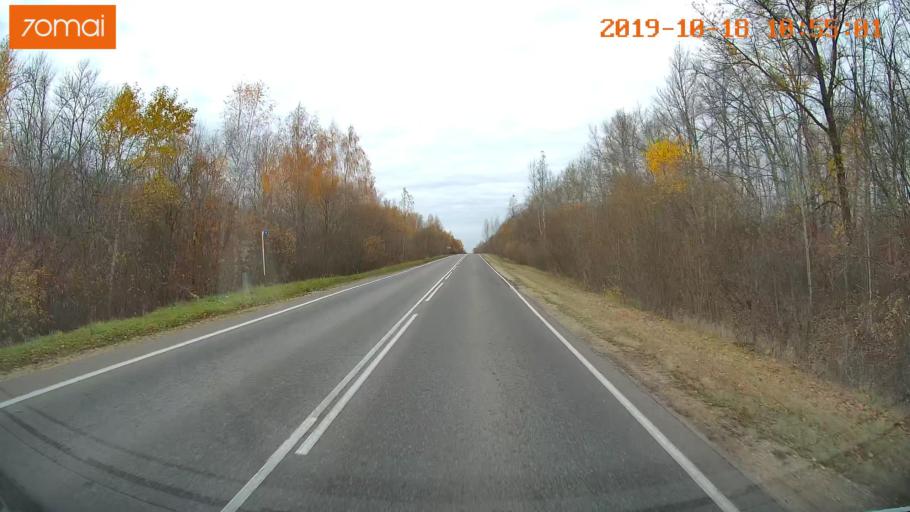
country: RU
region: Tula
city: Yepifan'
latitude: 53.7941
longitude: 38.6048
